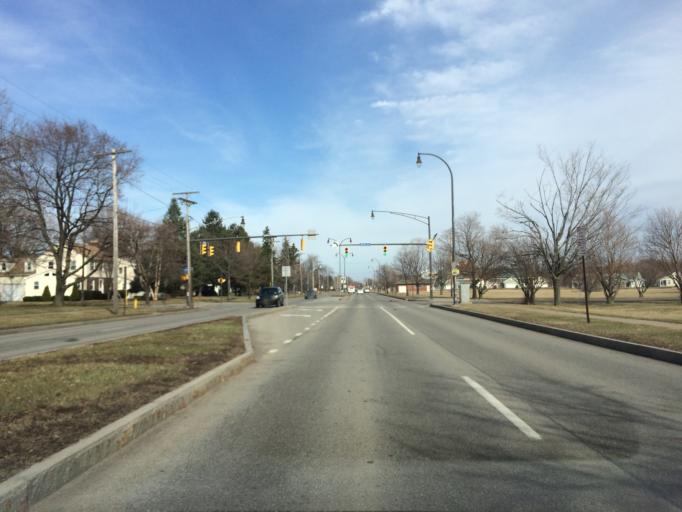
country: US
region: New York
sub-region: Monroe County
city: Rochester
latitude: 43.1250
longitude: -77.6075
